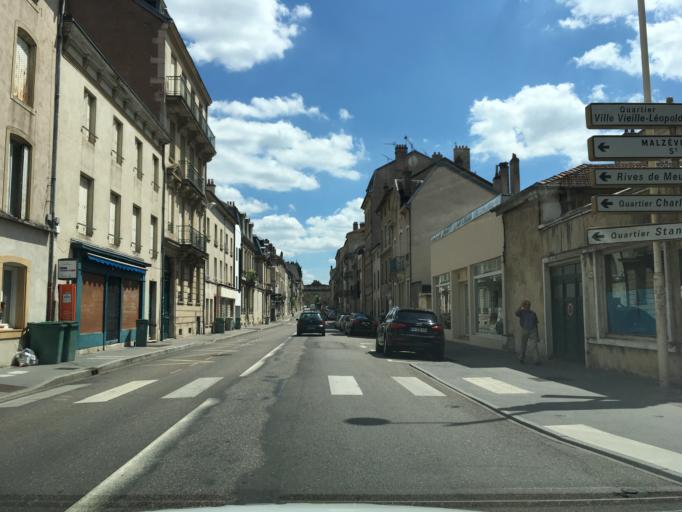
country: FR
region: Lorraine
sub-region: Departement de Meurthe-et-Moselle
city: Maxeville
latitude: 48.7010
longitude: 6.1720
